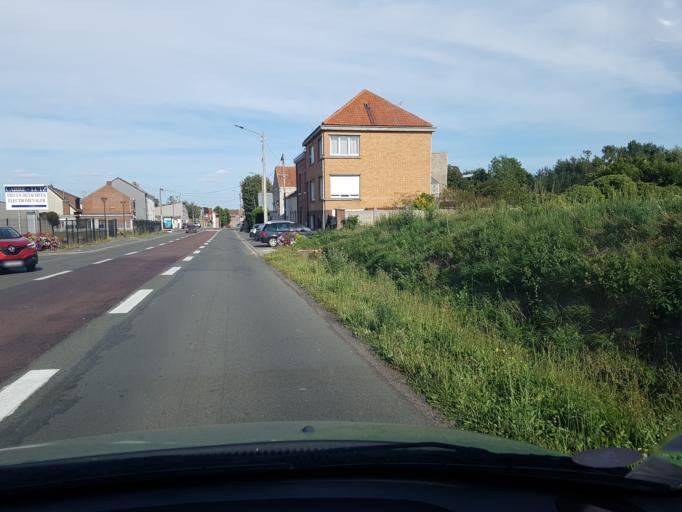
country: FR
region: Nord-Pas-de-Calais
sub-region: Departement du Pas-de-Calais
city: Vendin-les-Bethune
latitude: 50.5393
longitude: 2.5957
